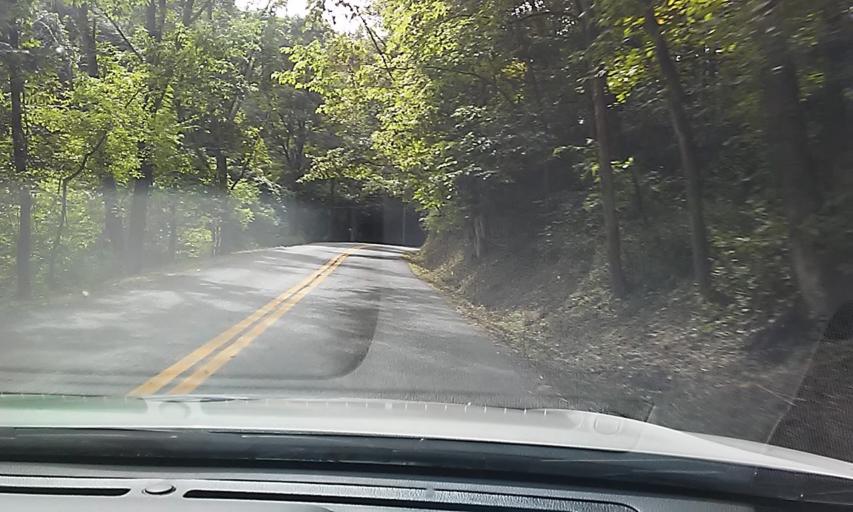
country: US
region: West Virginia
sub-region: Monongalia County
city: Star City
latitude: 39.6408
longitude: -80.0989
